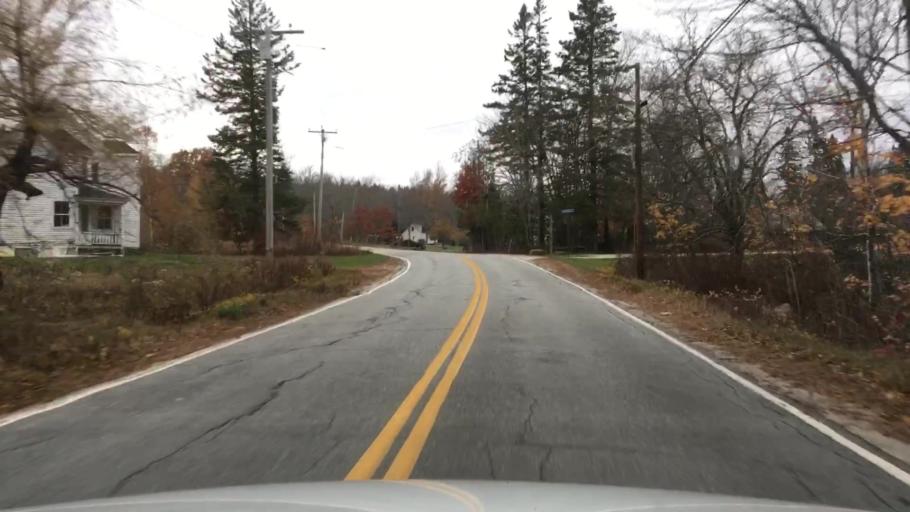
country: US
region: Maine
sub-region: Hancock County
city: Sedgwick
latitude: 44.3004
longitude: -68.5599
